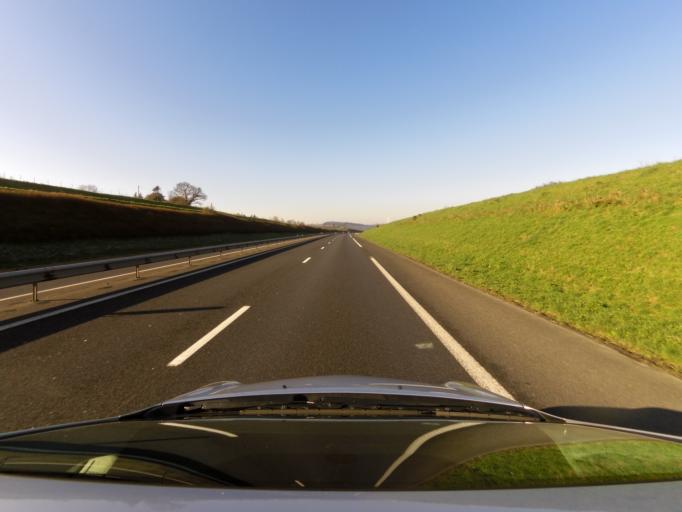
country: FR
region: Lower Normandy
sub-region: Departement du Calvados
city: Saint-Martin-des-Besaces
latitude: 48.9989
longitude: -0.9125
